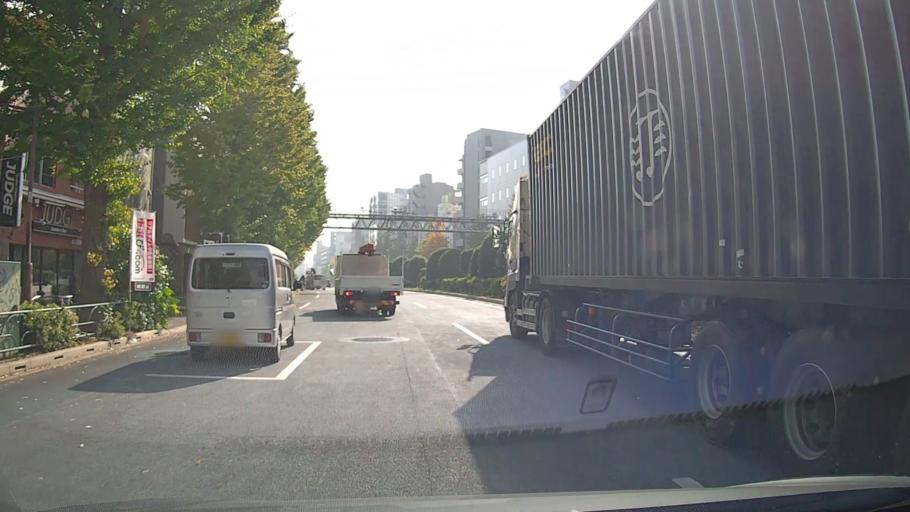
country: JP
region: Tokyo
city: Tokyo
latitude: 35.7241
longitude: 139.7467
